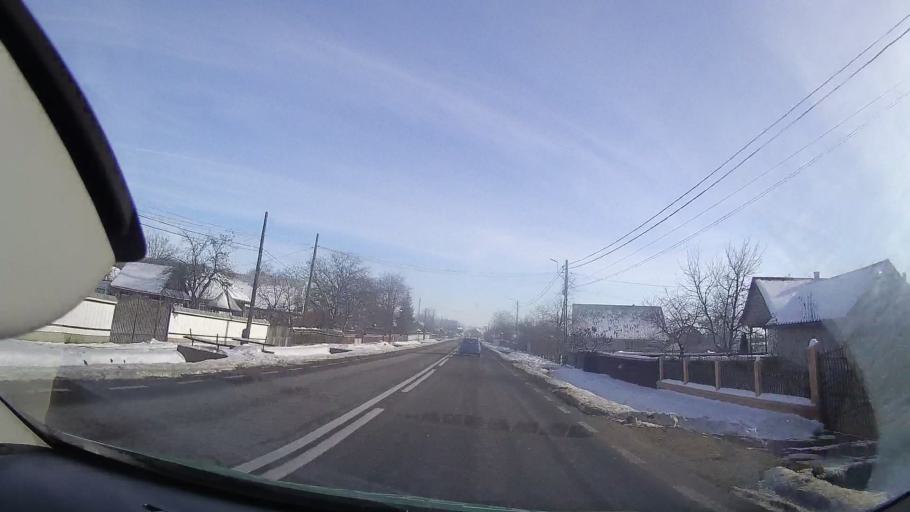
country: RO
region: Neamt
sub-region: Comuna Cracaoani
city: Cracaoani
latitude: 47.0891
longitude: 26.3257
